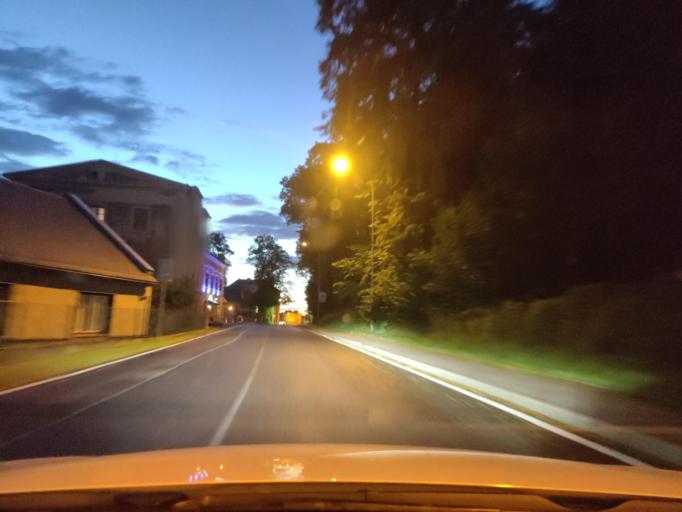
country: CZ
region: Olomoucky
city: Zlate Hory
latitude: 50.2580
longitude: 17.3993
